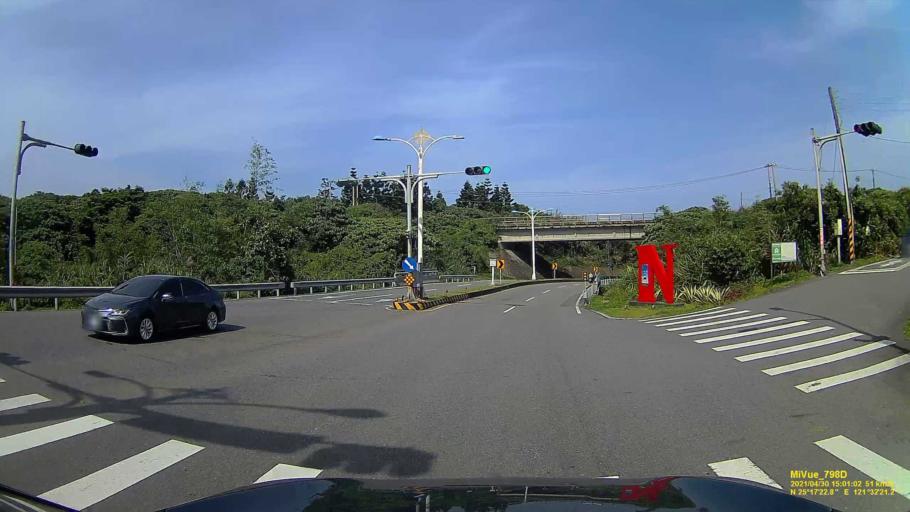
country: TW
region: Taipei
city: Taipei
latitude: 25.2897
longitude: 121.5395
